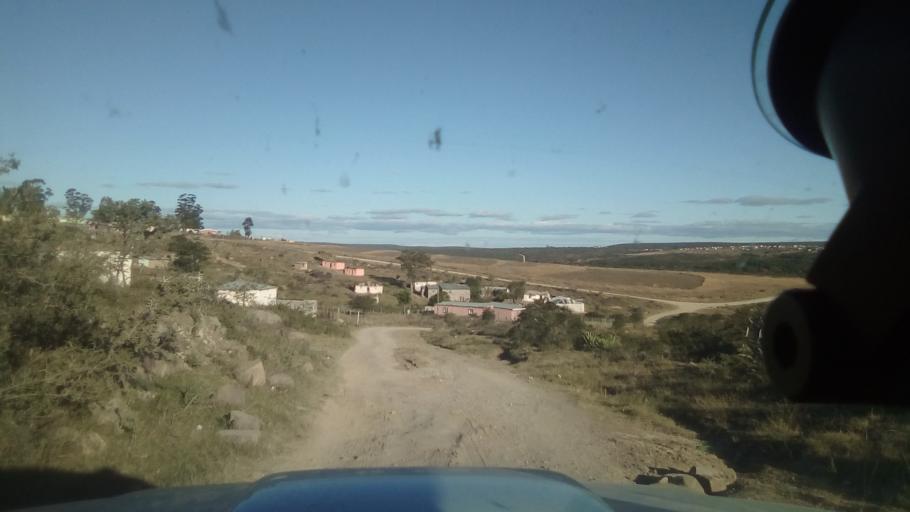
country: ZA
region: Eastern Cape
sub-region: Buffalo City Metropolitan Municipality
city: Bhisho
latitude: -32.7348
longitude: 27.3600
